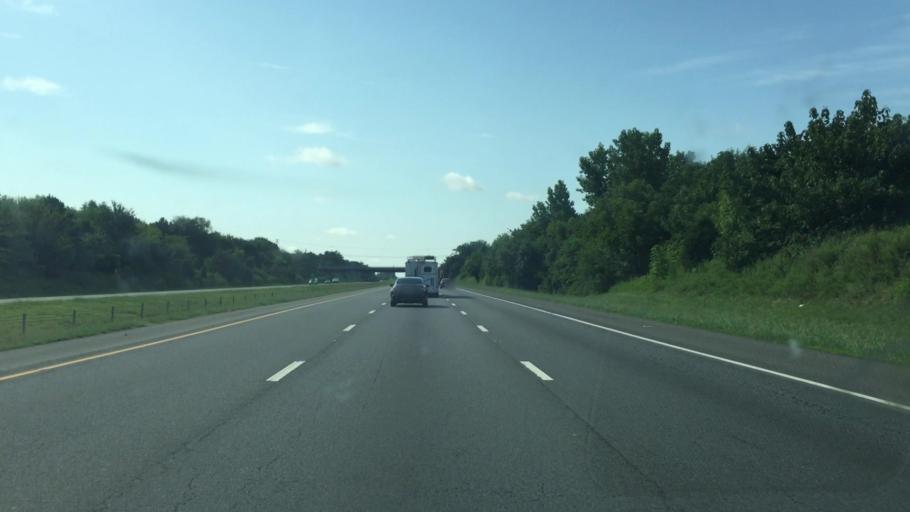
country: US
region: North Carolina
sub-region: Cabarrus County
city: Harrisburg
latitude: 35.3006
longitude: -80.6853
